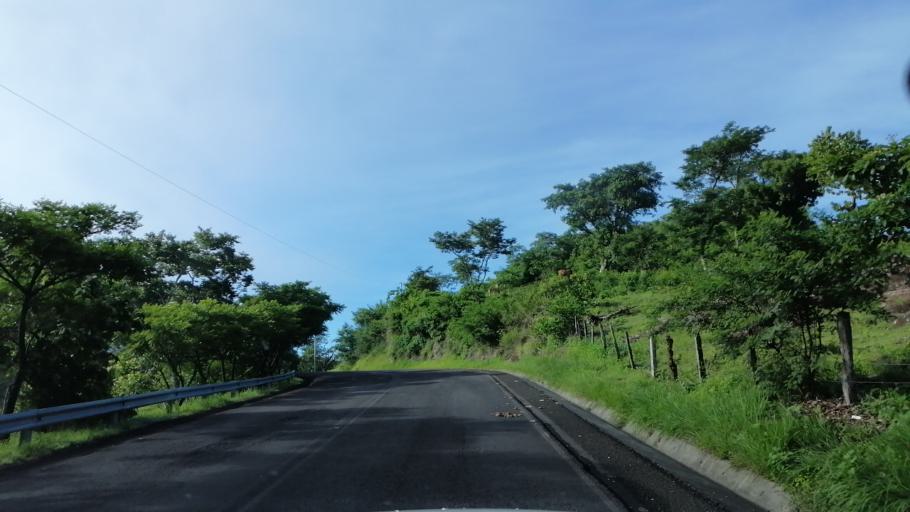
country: SV
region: Morazan
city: Cacaopera
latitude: 13.7871
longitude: -88.1108
